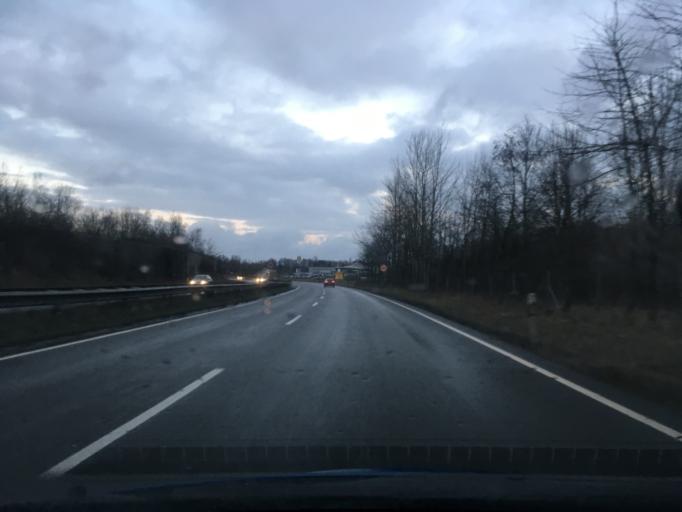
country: DE
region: Lower Saxony
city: Wendisch Evern
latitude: 53.2365
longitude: 10.4552
